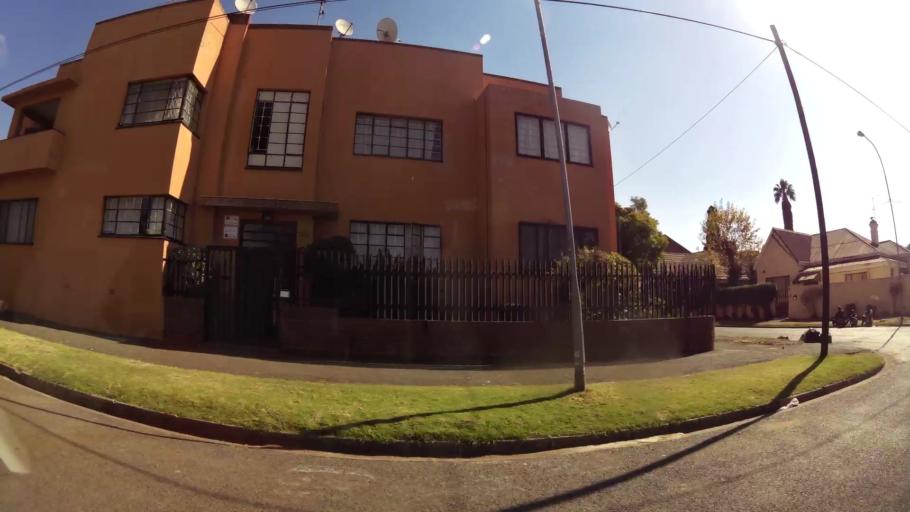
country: ZA
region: Gauteng
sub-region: City of Johannesburg Metropolitan Municipality
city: Johannesburg
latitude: -26.1765
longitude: 28.0726
